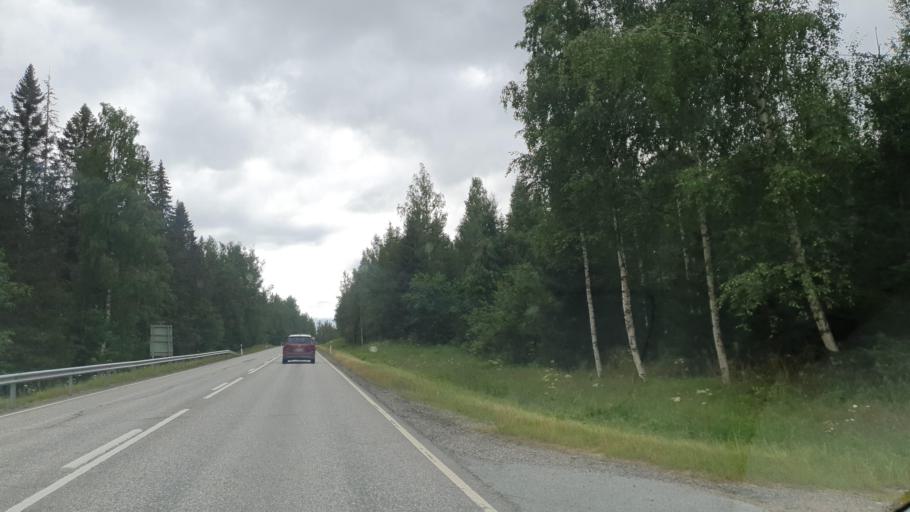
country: FI
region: Northern Savo
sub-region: Ylae-Savo
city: Sonkajaervi
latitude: 63.6876
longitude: 27.3432
